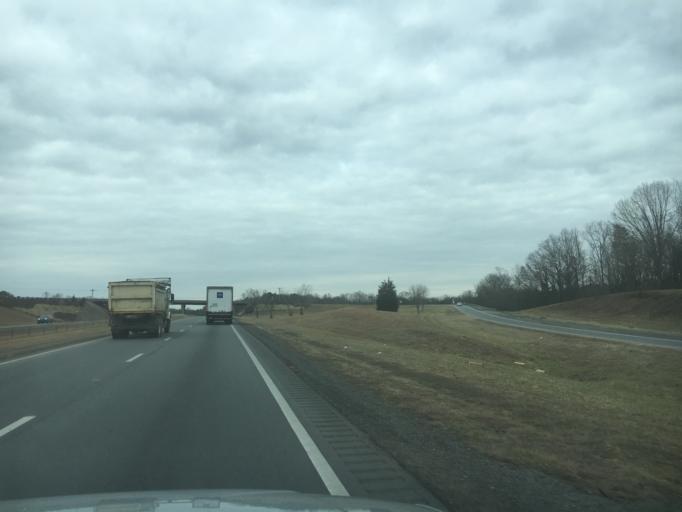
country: US
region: North Carolina
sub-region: Gaston County
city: Dallas
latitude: 35.3754
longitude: -81.2025
